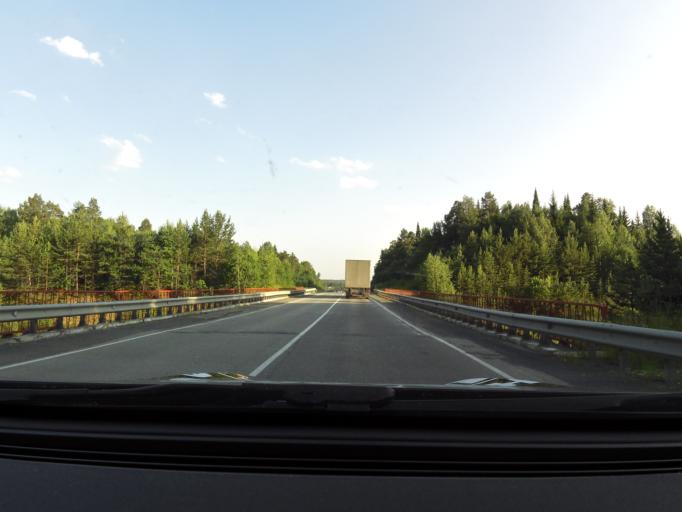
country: RU
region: Sverdlovsk
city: Druzhinino
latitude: 56.7993
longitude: 59.4631
